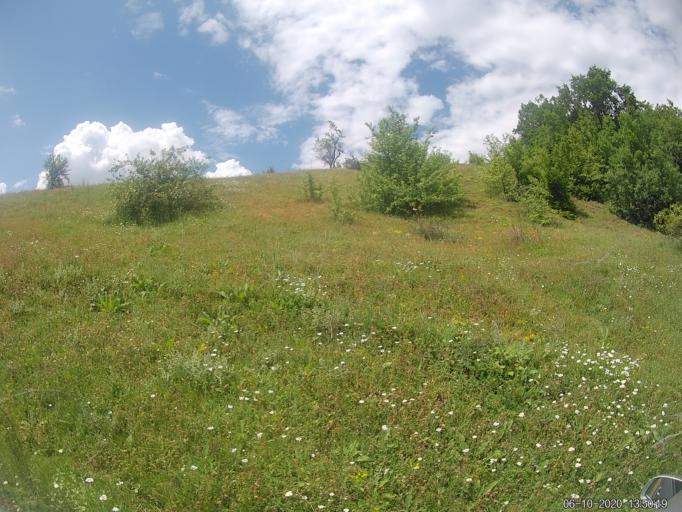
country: XK
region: Prizren
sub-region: Komuna e Therandes
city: Budakovo
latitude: 42.4063
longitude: 20.9242
